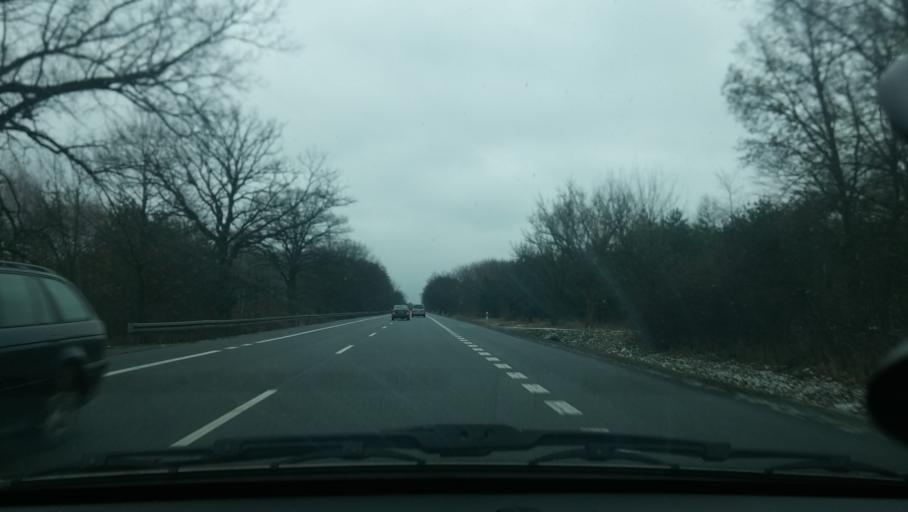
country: PL
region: Masovian Voivodeship
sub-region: Powiat wegrowski
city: Grebkow
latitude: 52.2094
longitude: 21.8838
